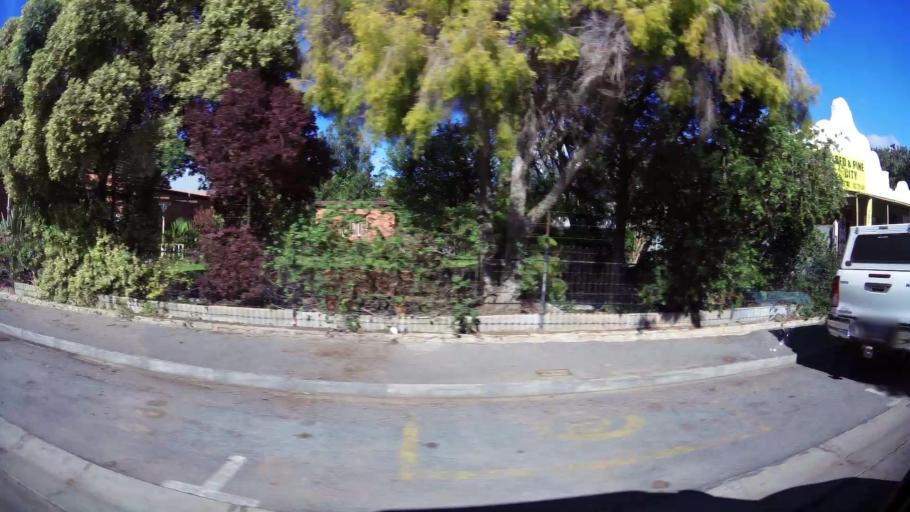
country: ZA
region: Western Cape
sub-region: Cape Winelands District Municipality
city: Ashton
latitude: -33.8019
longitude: 19.8838
